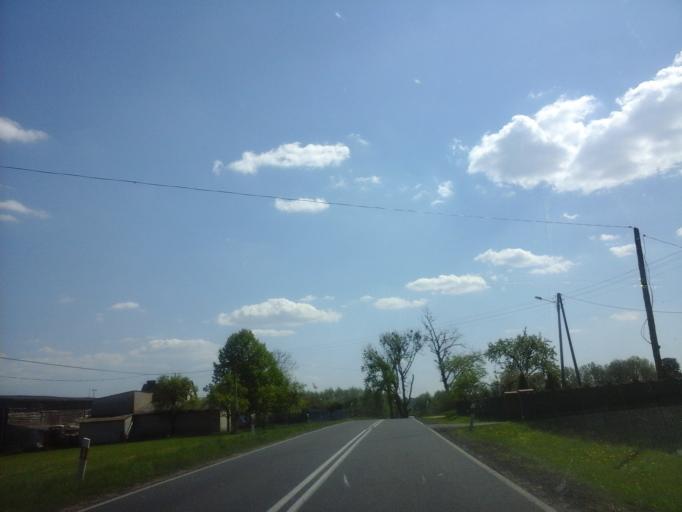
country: PL
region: Lubusz
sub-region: Powiat strzelecko-drezdenecki
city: Dobiegniew
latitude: 52.9872
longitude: 15.7498
